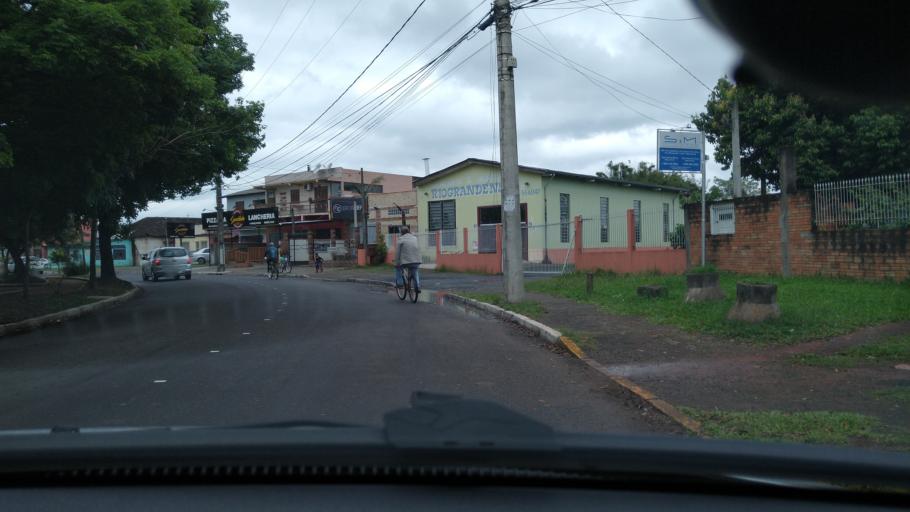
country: BR
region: Rio Grande do Sul
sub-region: Canoas
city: Canoas
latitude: -29.9023
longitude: -51.2056
